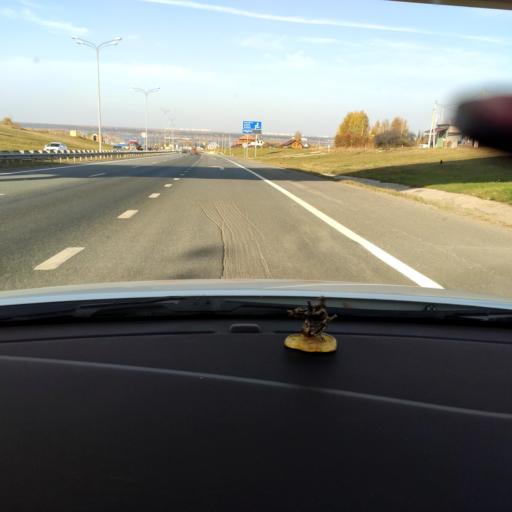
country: RU
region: Tatarstan
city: Osinovo
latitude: 55.7743
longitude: 48.8396
